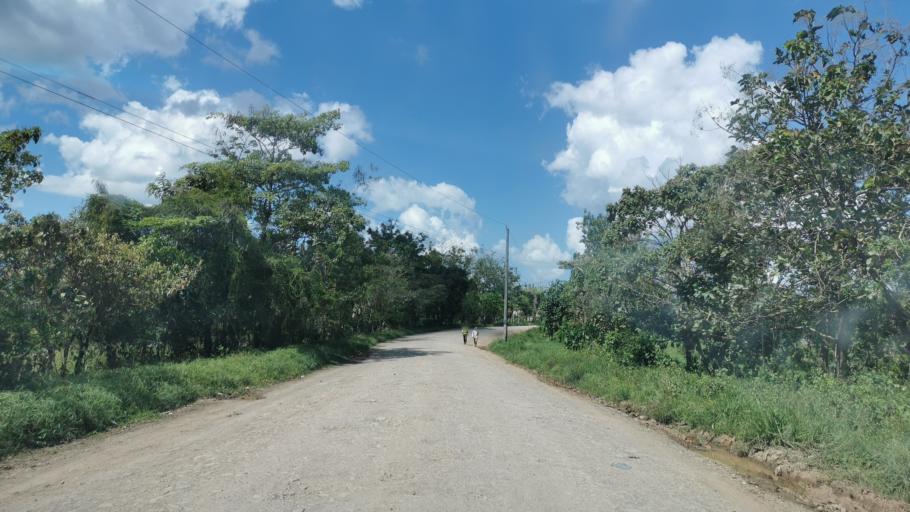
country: NI
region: Atlantico Sur
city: Rama
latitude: 12.1723
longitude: -84.2022
